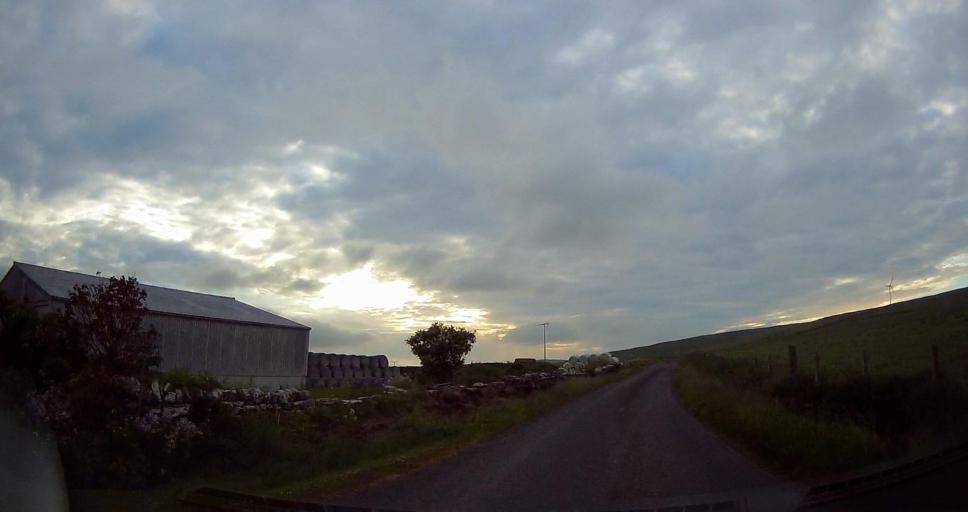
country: GB
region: Scotland
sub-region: Orkney Islands
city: Stromness
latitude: 59.0947
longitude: -3.1884
